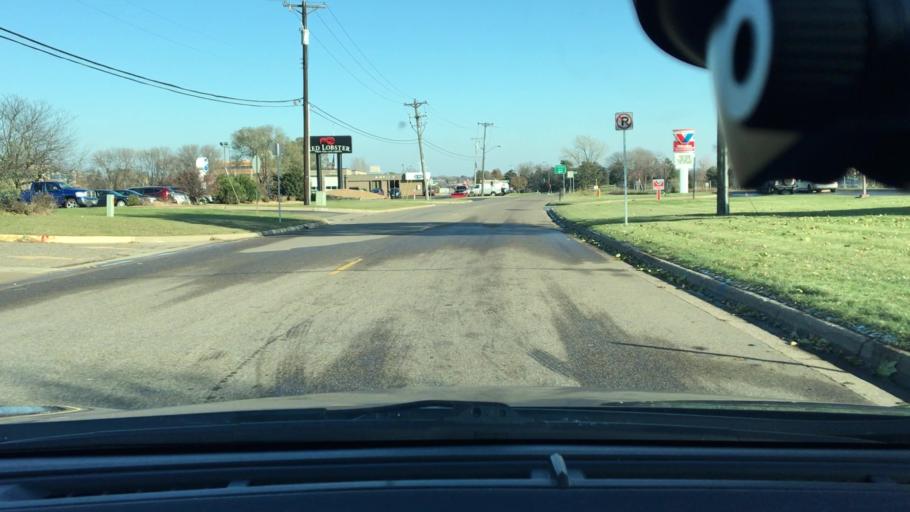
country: US
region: Minnesota
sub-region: Hennepin County
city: Golden Valley
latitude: 44.9847
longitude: -93.3943
